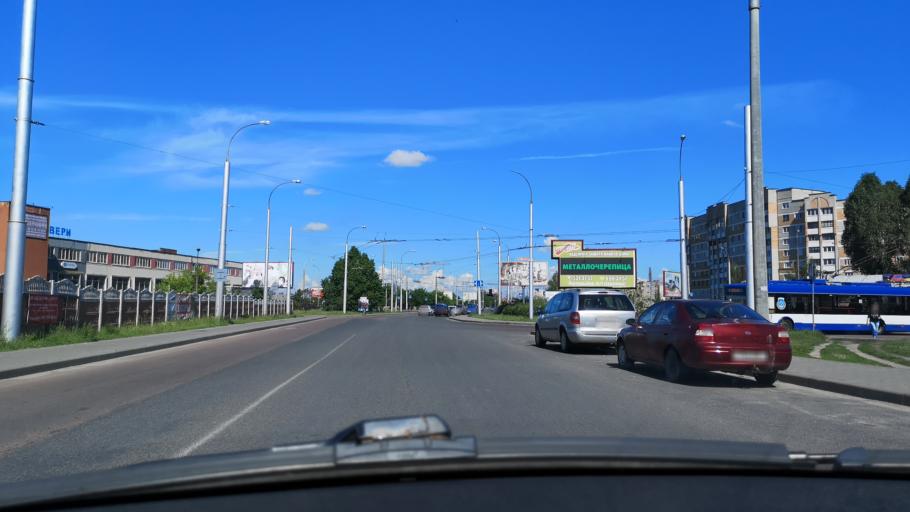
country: BY
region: Brest
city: Brest
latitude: 52.0695
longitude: 23.7516
